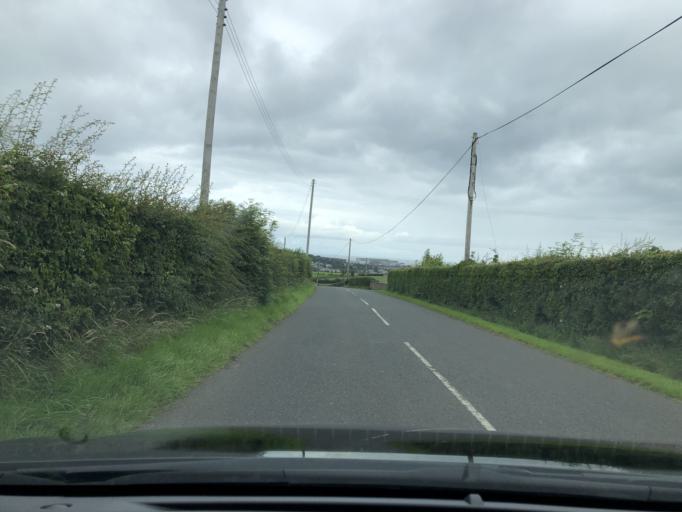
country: GB
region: Northern Ireland
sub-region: Larne District
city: Larne
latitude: 54.8401
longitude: -5.8376
